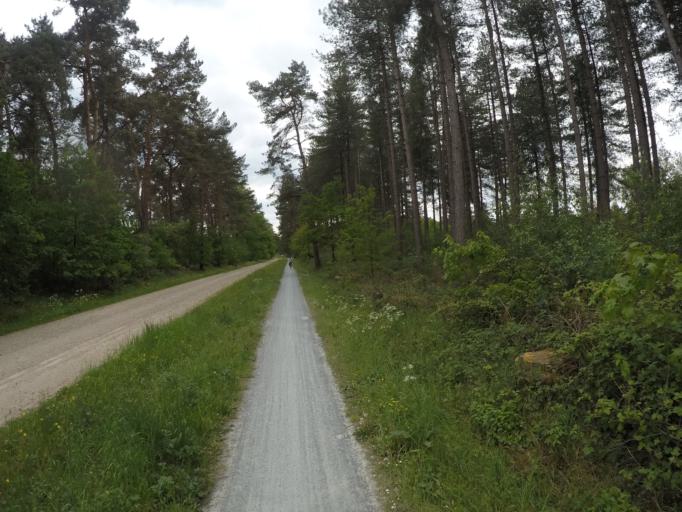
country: BE
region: Flanders
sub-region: Provincie Antwerpen
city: Oostmalle
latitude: 51.2821
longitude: 4.7418
